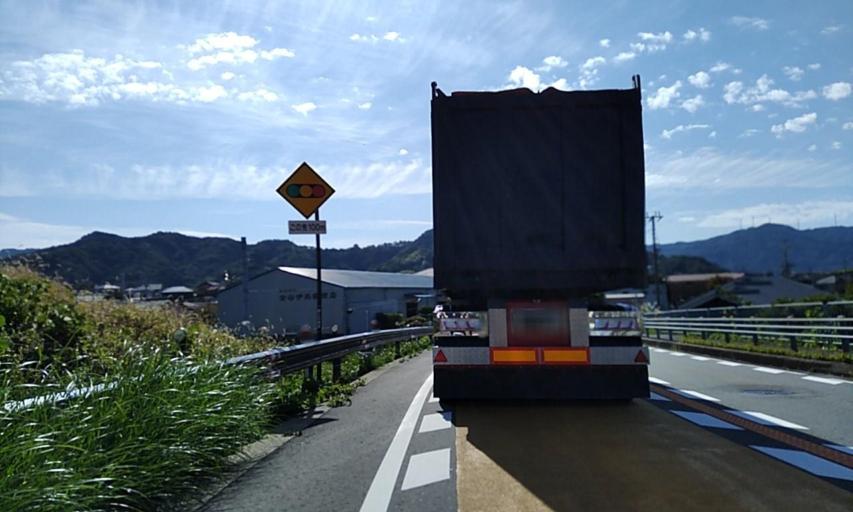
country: JP
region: Wakayama
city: Kainan
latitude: 34.0360
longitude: 135.1852
